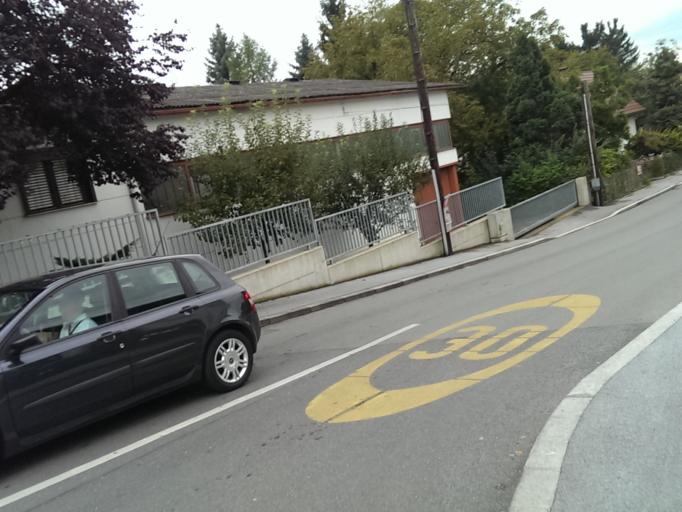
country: AT
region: Styria
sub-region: Politischer Bezirk Graz-Umgebung
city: Raaba
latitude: 47.0506
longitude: 15.4790
